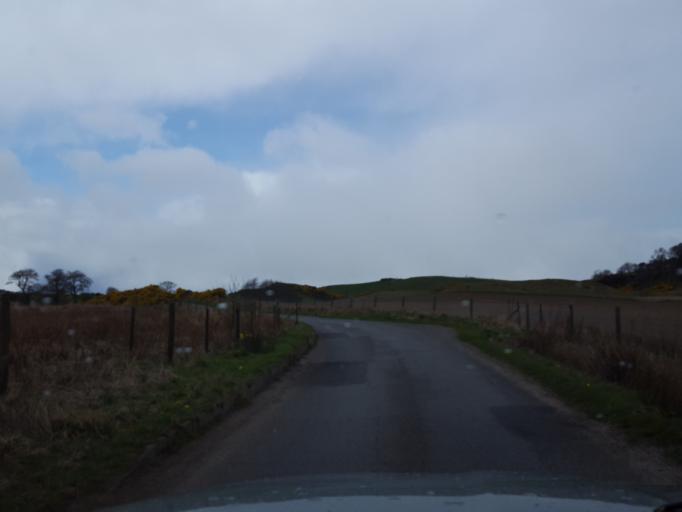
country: GB
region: Scotland
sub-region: Perth and Kinross
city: Errol
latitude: 56.4374
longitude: -3.3040
